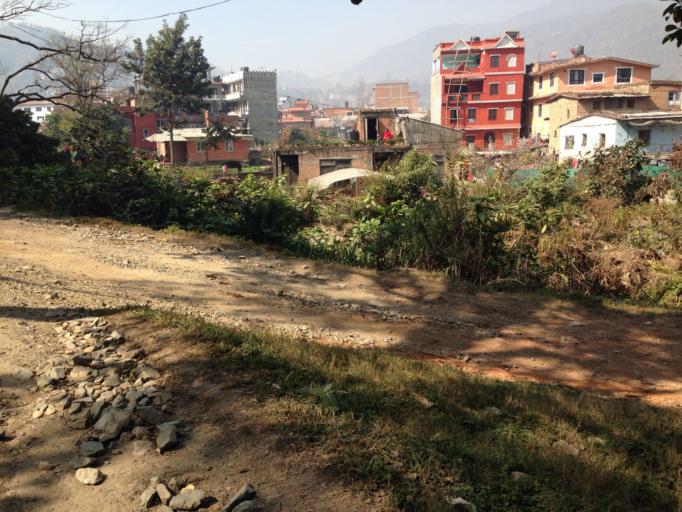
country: NP
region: Central Region
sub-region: Bagmati Zone
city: Kathmandu
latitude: 27.7182
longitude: 85.2891
